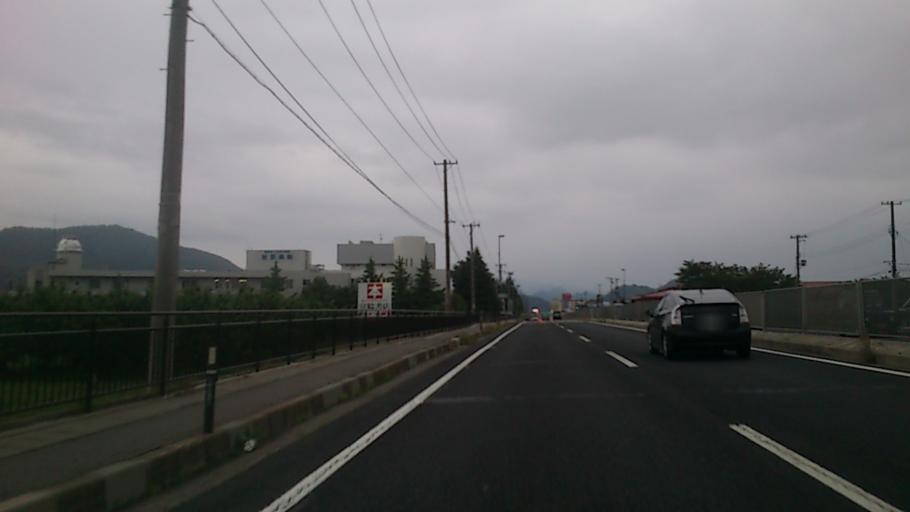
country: JP
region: Yamagata
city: Tendo
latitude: 38.3833
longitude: 140.3821
